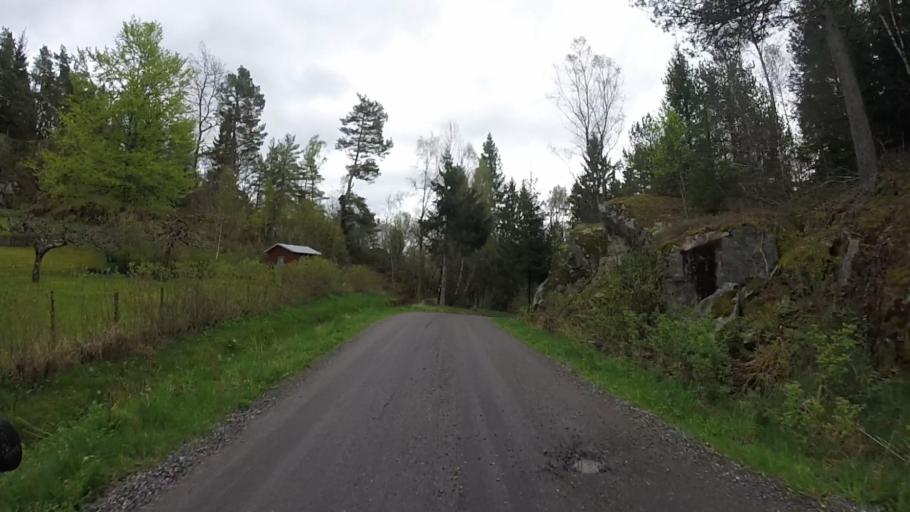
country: SE
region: Vaestra Goetaland
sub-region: Trollhattan
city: Sjuntorp
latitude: 58.2063
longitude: 12.2115
